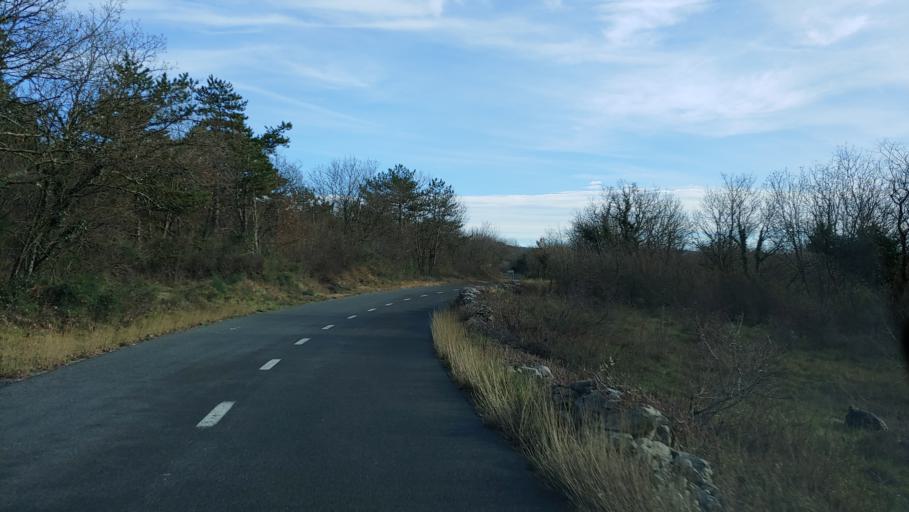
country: IT
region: Friuli Venezia Giulia
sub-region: Provincia di Trieste
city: Sistiana-Visogliano
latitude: 45.8131
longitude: 13.6682
